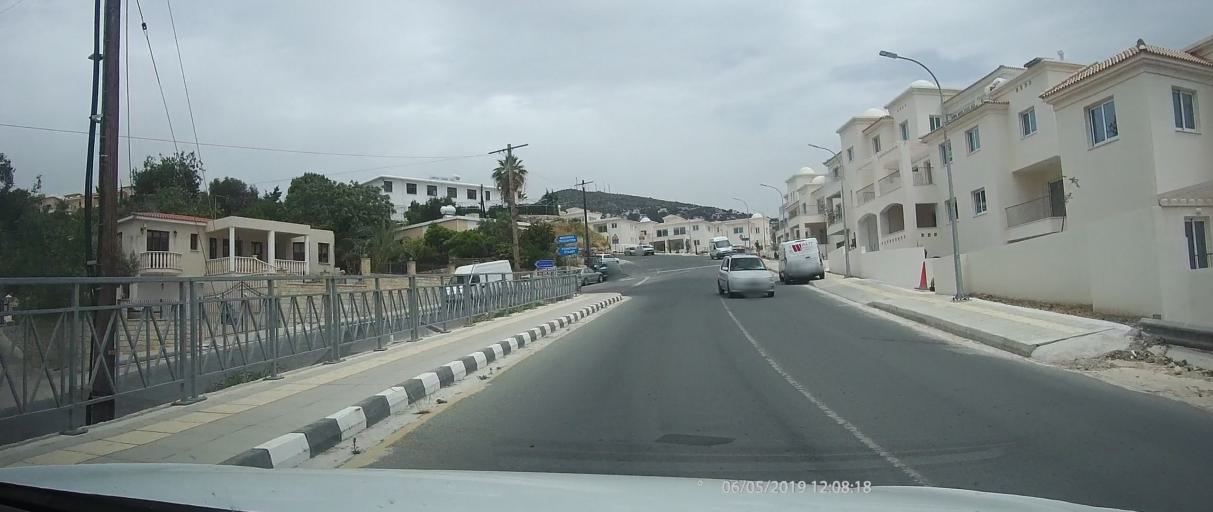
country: CY
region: Pafos
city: Tala
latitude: 34.8335
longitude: 32.4294
